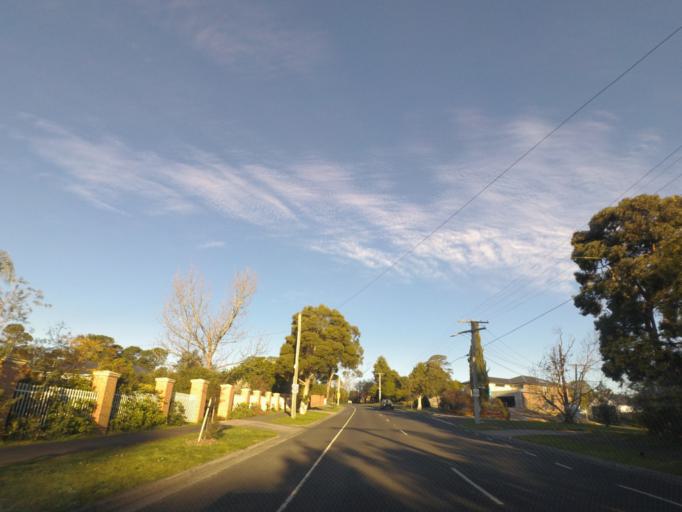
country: AU
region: Victoria
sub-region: Manningham
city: Park Orchards
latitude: -37.7820
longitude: 145.2258
